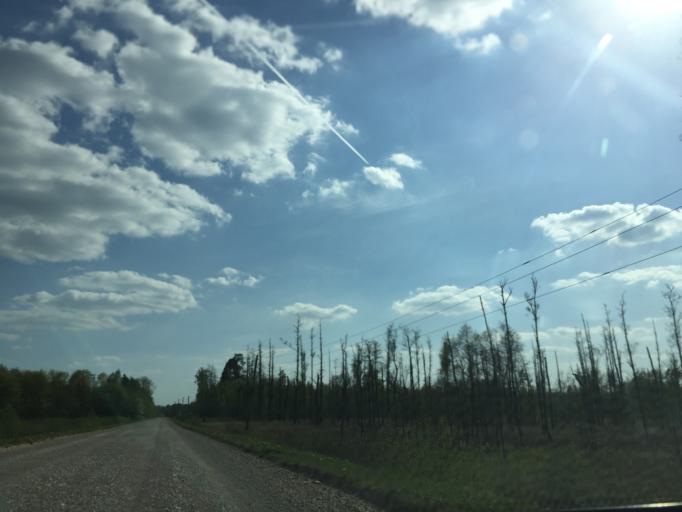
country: LV
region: Vecumnieki
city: Vecumnieki
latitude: 56.5241
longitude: 24.4147
